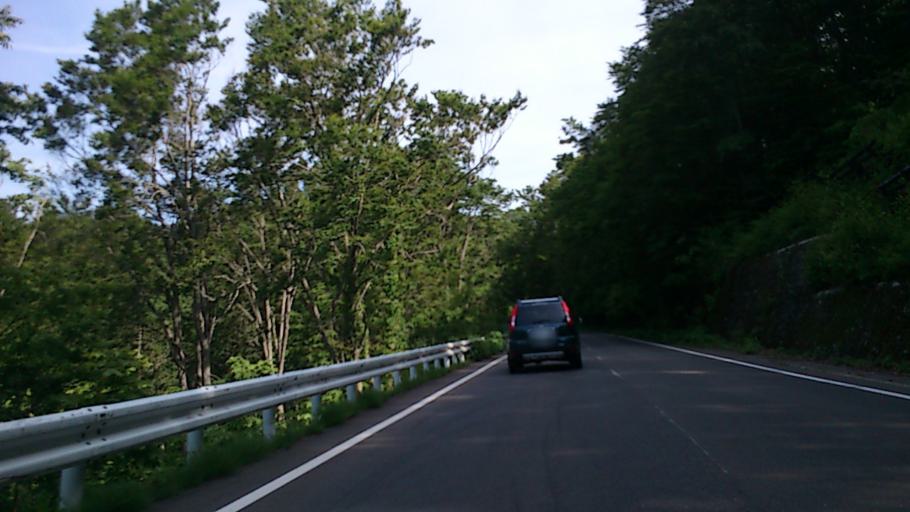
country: JP
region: Aomori
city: Aomori Shi
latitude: 40.7023
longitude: 140.8292
